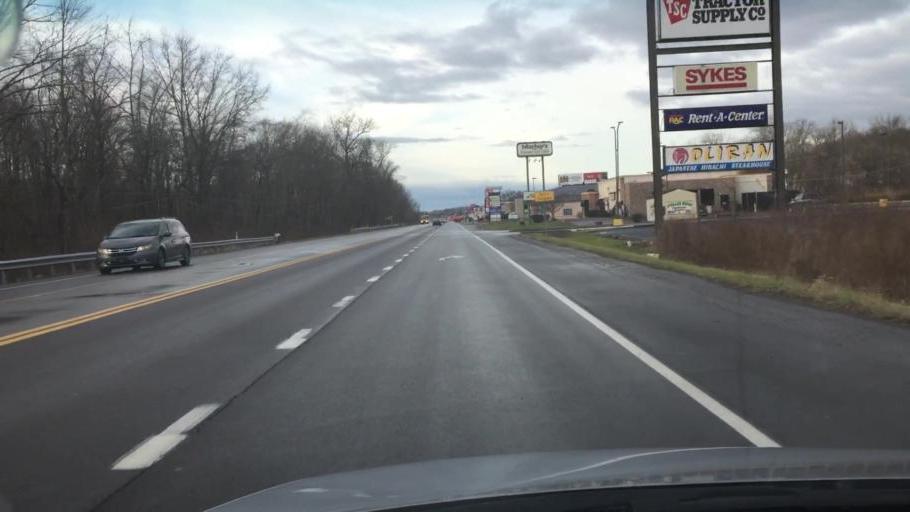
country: US
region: Pennsylvania
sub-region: Columbia County
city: Espy
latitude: 41.0068
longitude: -76.4296
